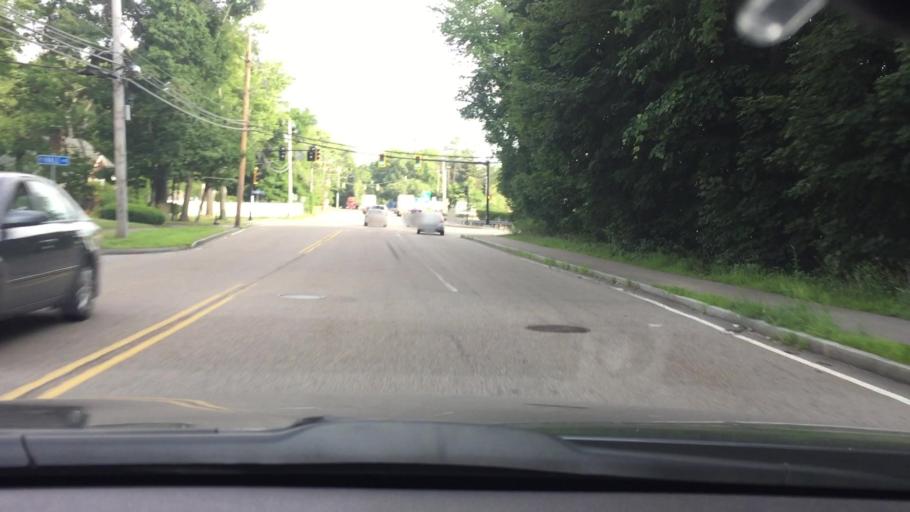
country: US
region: Massachusetts
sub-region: Norfolk County
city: Sharon
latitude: 42.1525
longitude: -71.2037
